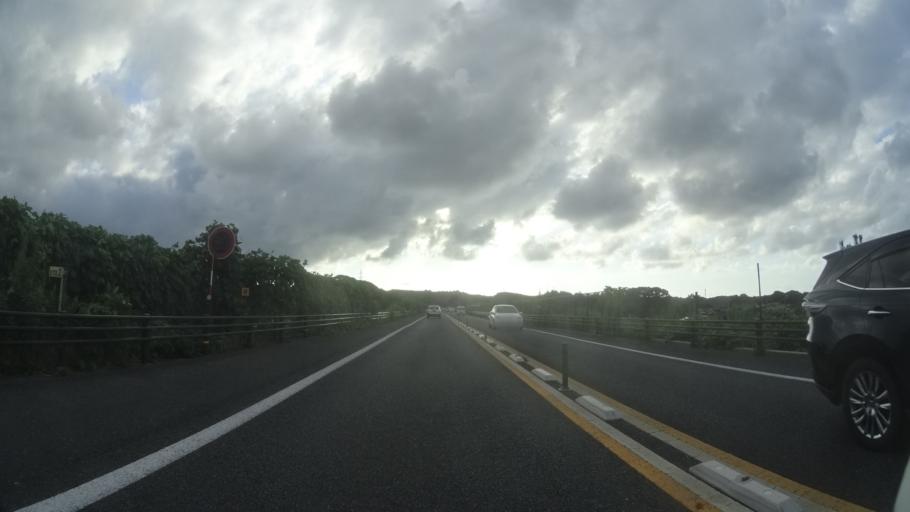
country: JP
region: Tottori
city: Kurayoshi
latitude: 35.5080
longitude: 133.6240
